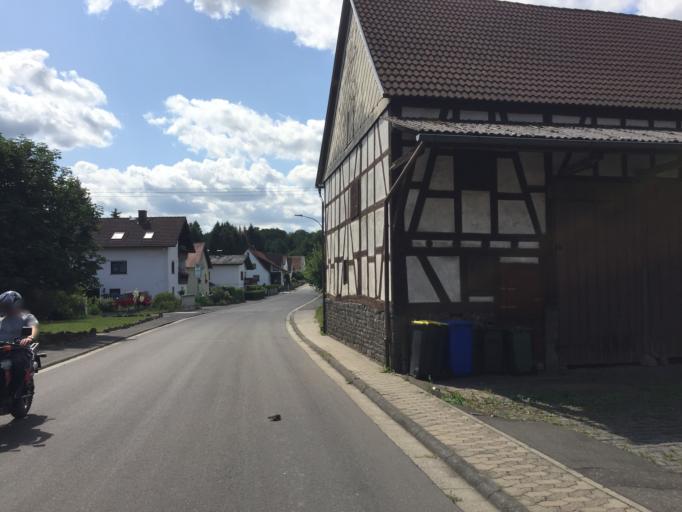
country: DE
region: Hesse
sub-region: Regierungsbezirk Giessen
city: Grunberg
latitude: 50.5700
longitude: 8.9680
